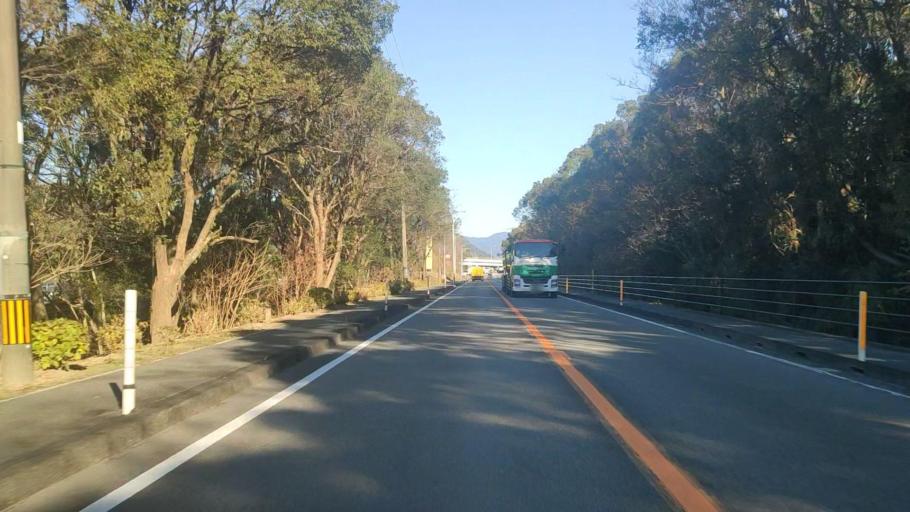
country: JP
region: Miyazaki
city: Nobeoka
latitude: 32.5326
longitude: 131.6806
